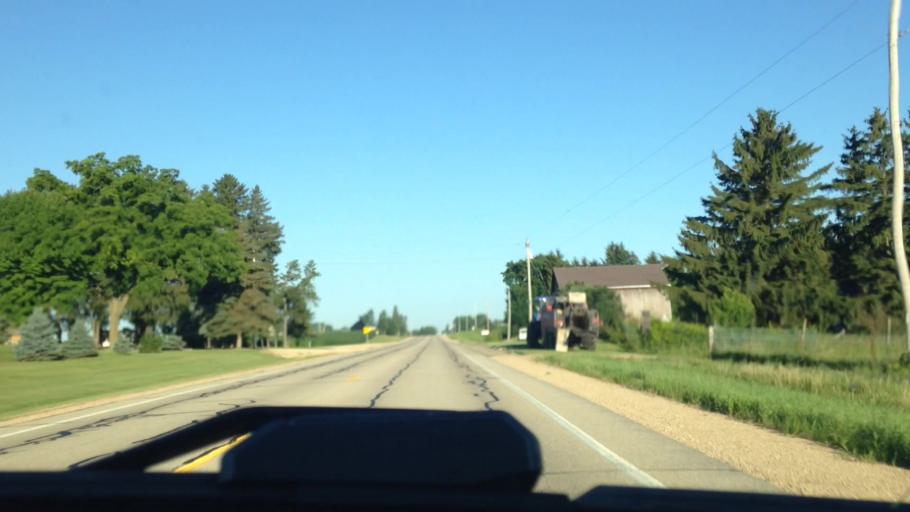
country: US
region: Wisconsin
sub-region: Columbia County
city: Fall River
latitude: 43.3413
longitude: -89.0832
